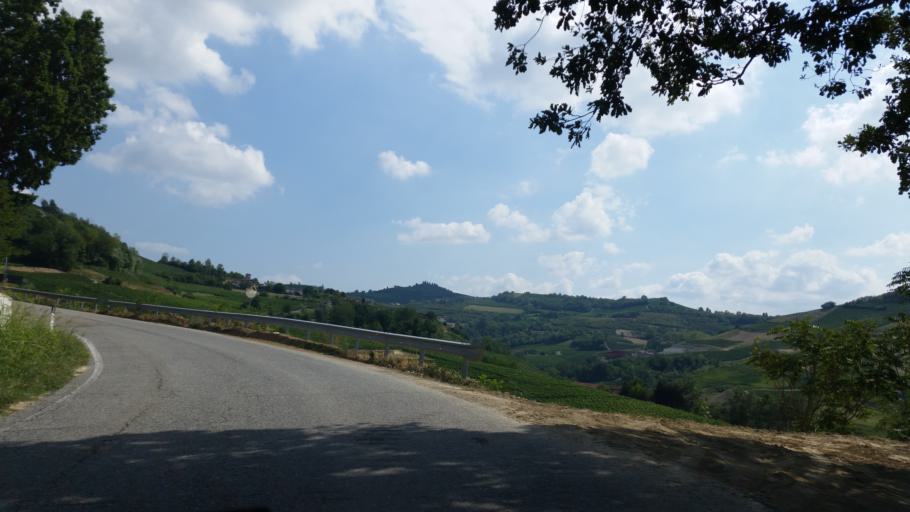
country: IT
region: Piedmont
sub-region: Provincia di Cuneo
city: Bricco di Neive
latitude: 44.6983
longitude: 8.1348
